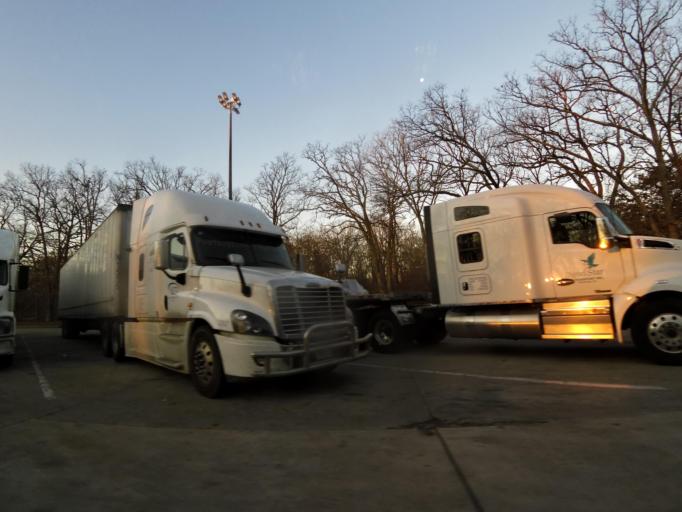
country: US
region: Illinois
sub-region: Marion County
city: Salem
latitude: 38.5968
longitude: -88.9643
